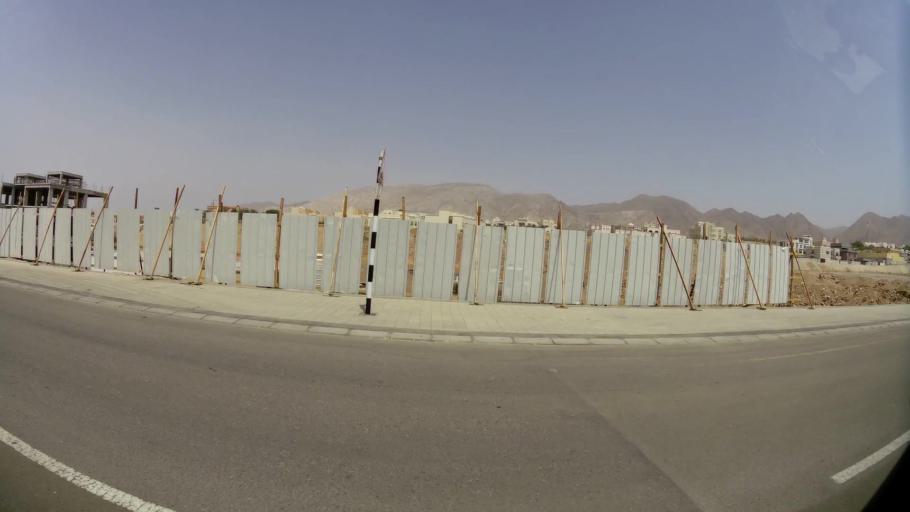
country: OM
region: Muhafazat Masqat
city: Bawshar
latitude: 23.5560
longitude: 58.3932
